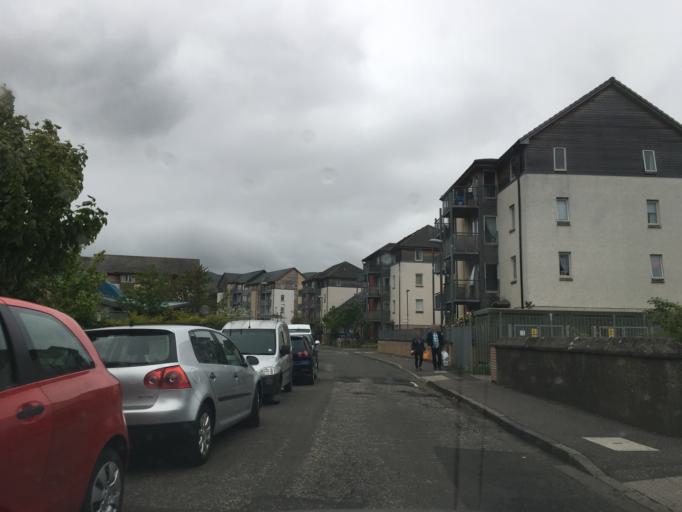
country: GB
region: Scotland
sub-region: Edinburgh
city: Colinton
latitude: 55.9124
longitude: -3.2232
